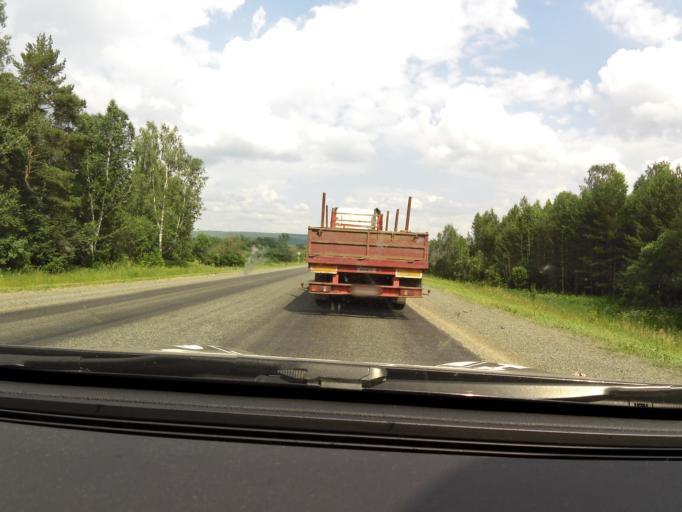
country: RU
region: Sverdlovsk
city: Ufimskiy
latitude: 56.7882
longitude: 58.3287
